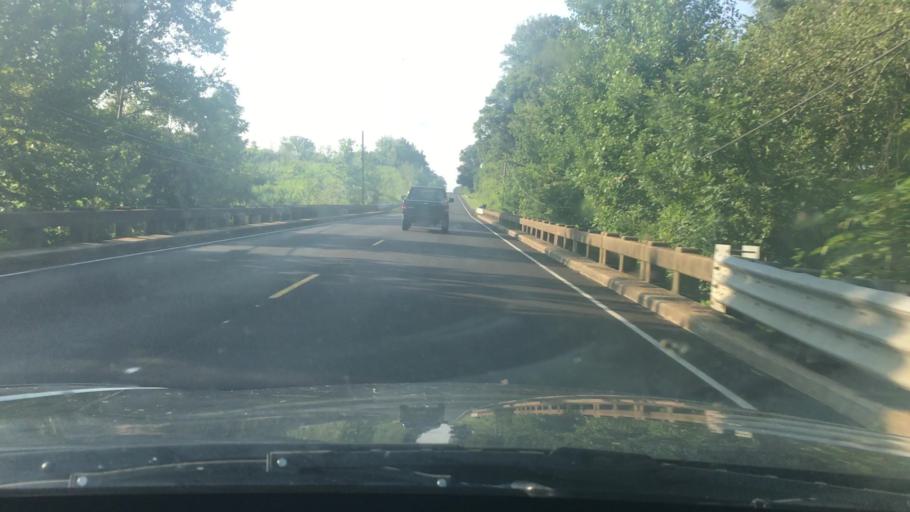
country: US
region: Virginia
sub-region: City of Danville
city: Danville
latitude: 36.5047
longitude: -79.3889
